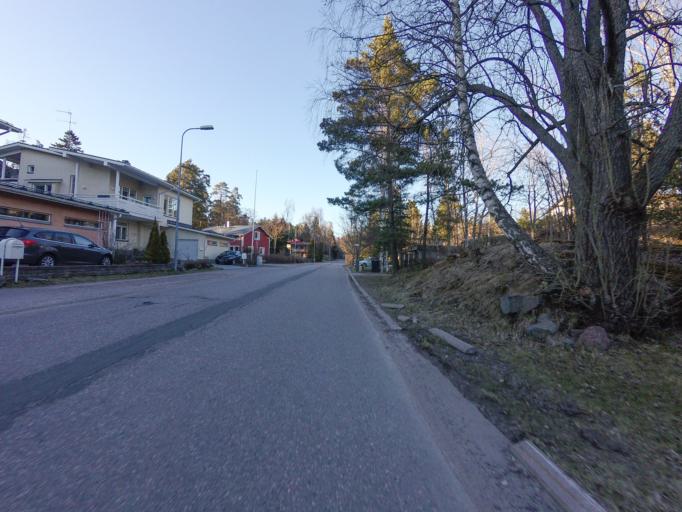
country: FI
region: Uusimaa
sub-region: Helsinki
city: Helsinki
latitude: 60.1747
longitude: 25.0240
